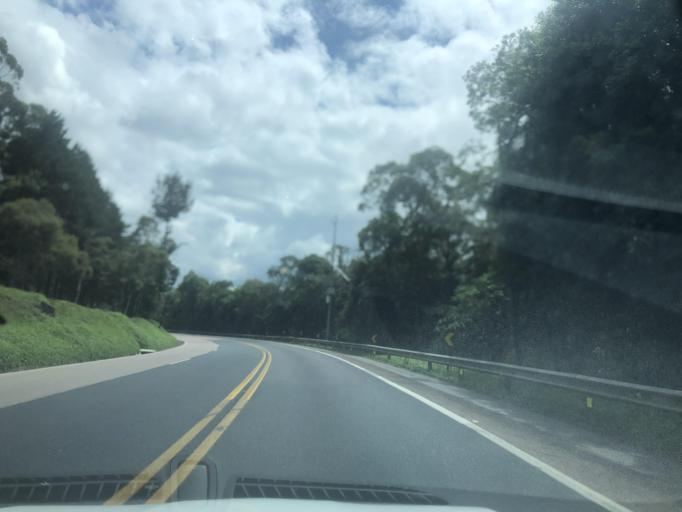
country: BR
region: Parana
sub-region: Rio Negro
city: Rio Negro
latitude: -26.0397
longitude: -49.6993
